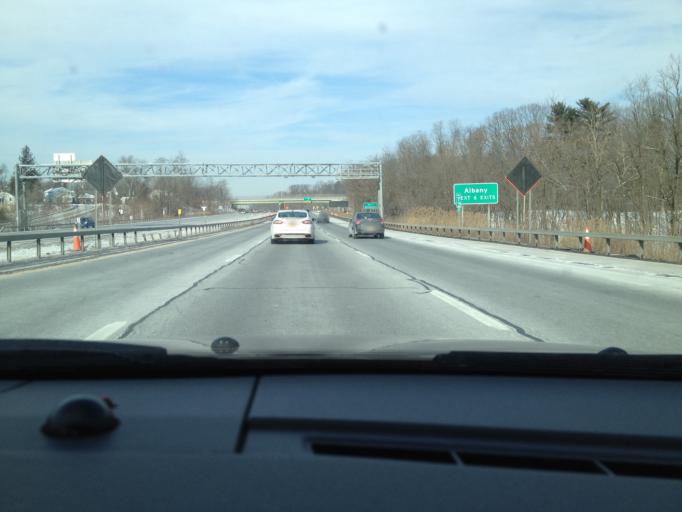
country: US
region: New York
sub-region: Rensselaer County
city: Rensselaer
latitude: 42.6571
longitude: -73.7197
